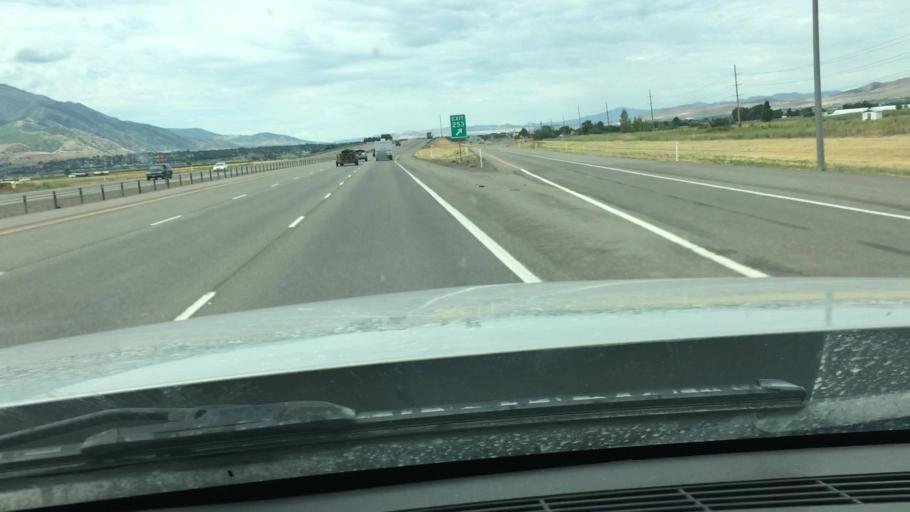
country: US
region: Utah
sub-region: Utah County
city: Benjamin
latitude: 40.0897
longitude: -111.6986
